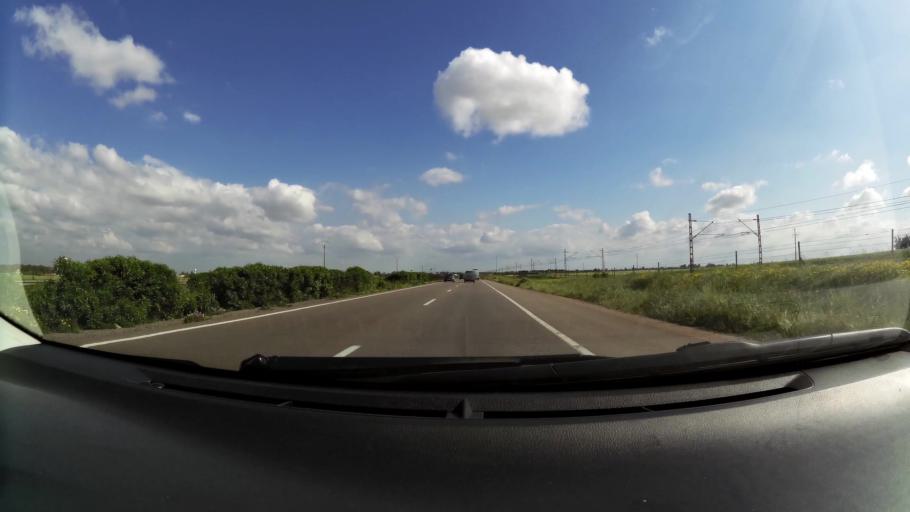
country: MA
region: Chaouia-Ouardigha
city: Nouaseur
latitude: 33.3512
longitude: -7.6161
